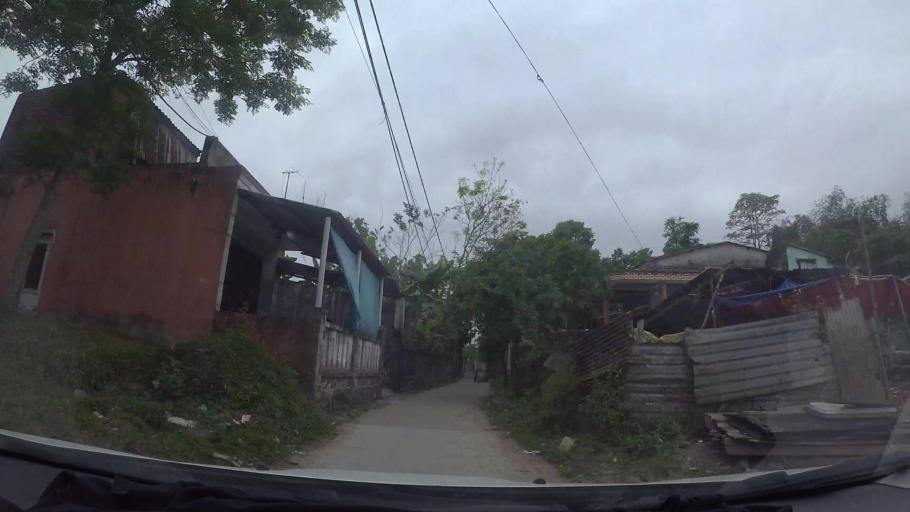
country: VN
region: Da Nang
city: Lien Chieu
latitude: 16.0783
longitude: 108.0969
